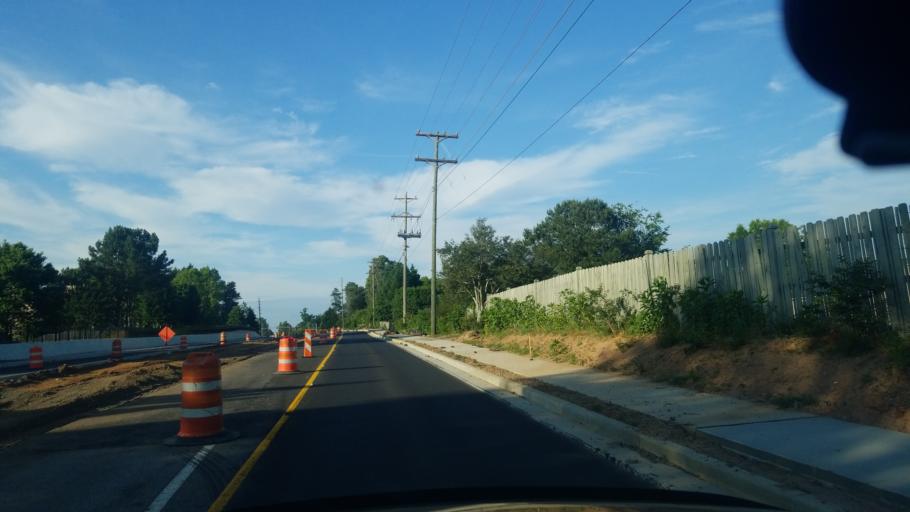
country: US
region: Georgia
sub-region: Fulton County
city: Johns Creek
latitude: 34.0876
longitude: -84.1830
